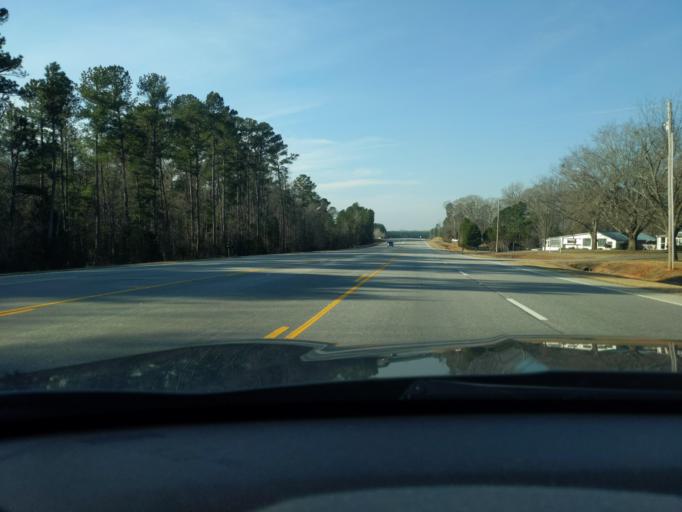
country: US
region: South Carolina
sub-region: Abbeville County
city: Abbeville
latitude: 34.1189
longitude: -82.4592
